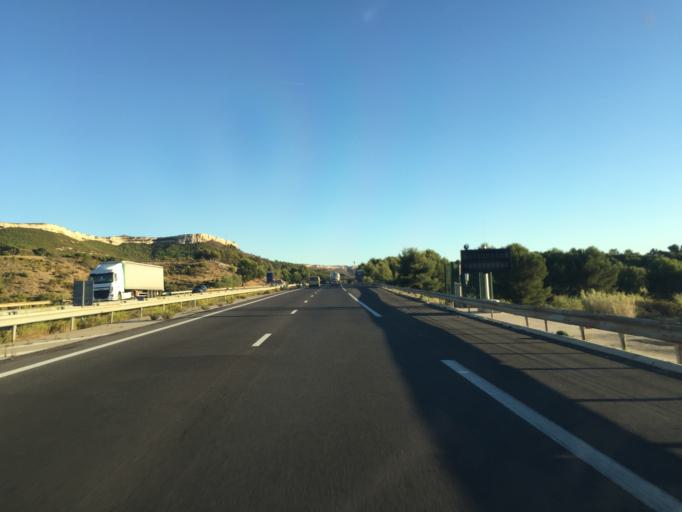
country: FR
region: Provence-Alpes-Cote d'Azur
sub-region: Departement des Bouches-du-Rhone
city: Rognac
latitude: 43.5032
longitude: 5.2376
